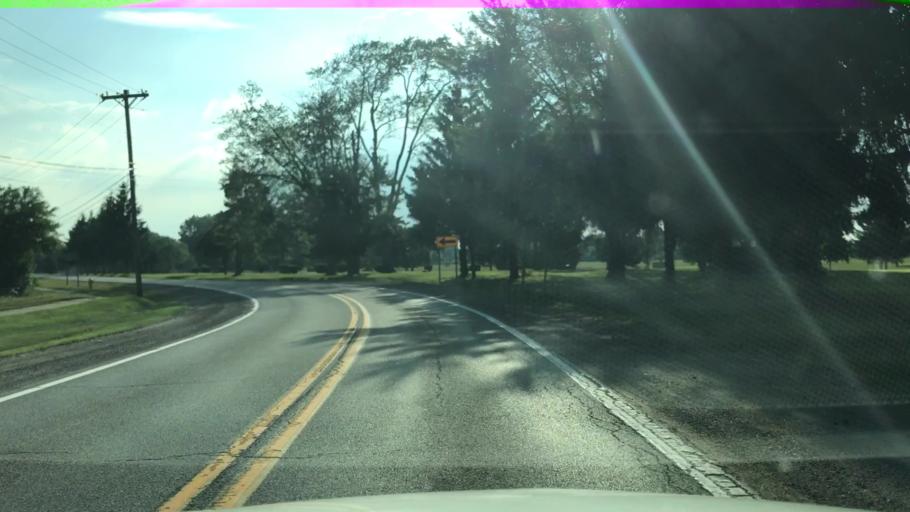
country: US
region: Michigan
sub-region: Macomb County
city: Clinton
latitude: 42.5790
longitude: -82.9553
